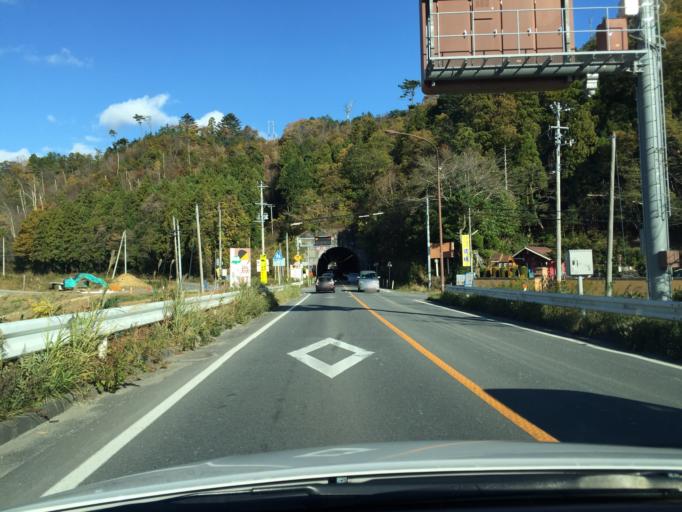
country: JP
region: Fukushima
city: Iwaki
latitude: 37.1603
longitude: 140.9951
